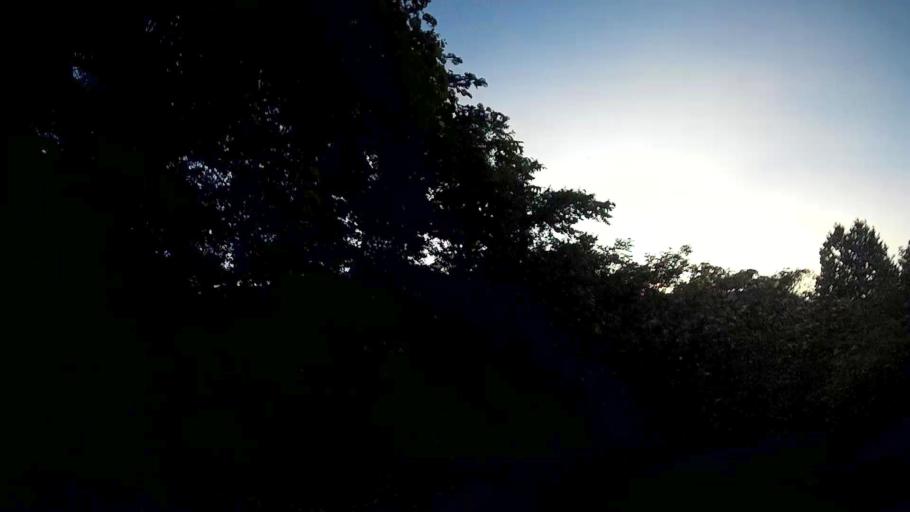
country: JP
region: Hokkaido
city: Iwanai
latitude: 42.6429
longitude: 140.0332
